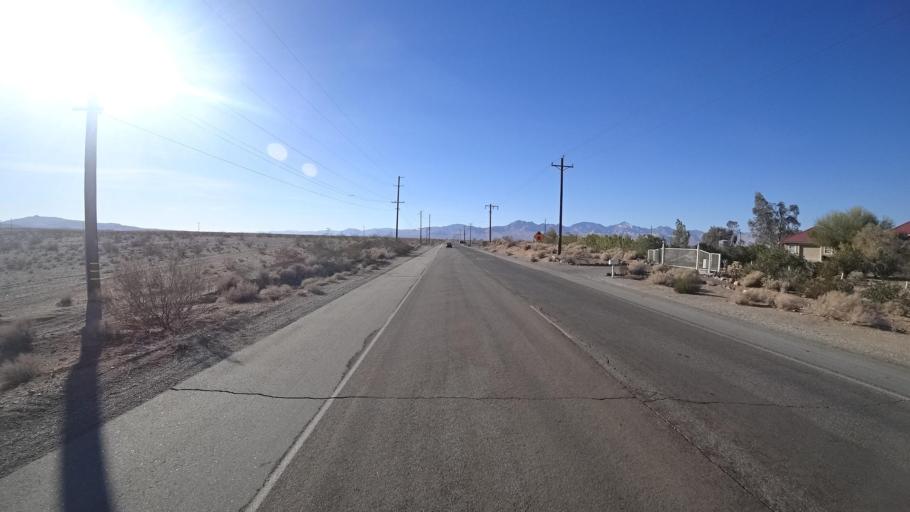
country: US
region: California
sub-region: Kern County
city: China Lake Acres
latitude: 35.6225
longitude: -117.7203
